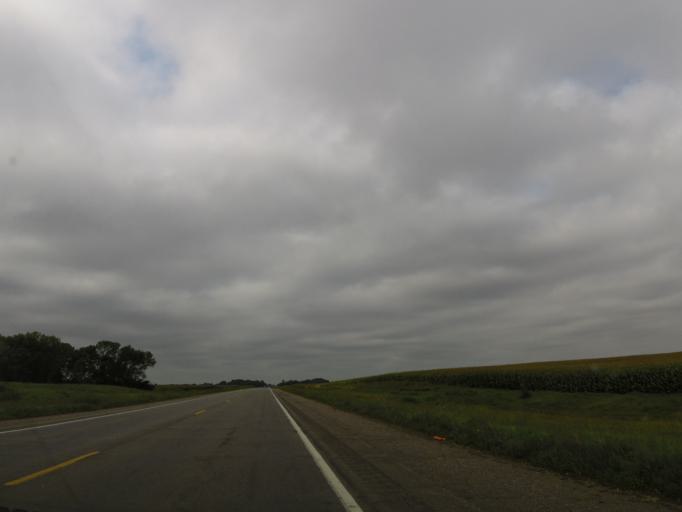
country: US
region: Minnesota
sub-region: Renville County
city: Renville
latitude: 44.7891
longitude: -95.2279
